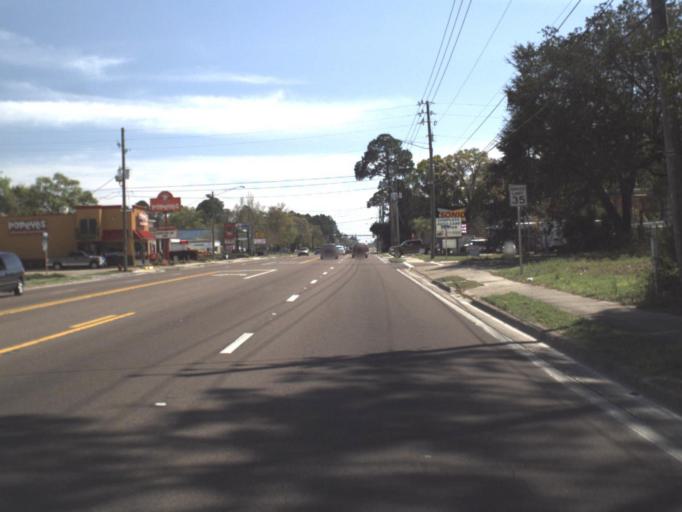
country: US
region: Florida
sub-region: Bay County
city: Lynn Haven
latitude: 30.2367
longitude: -85.6489
